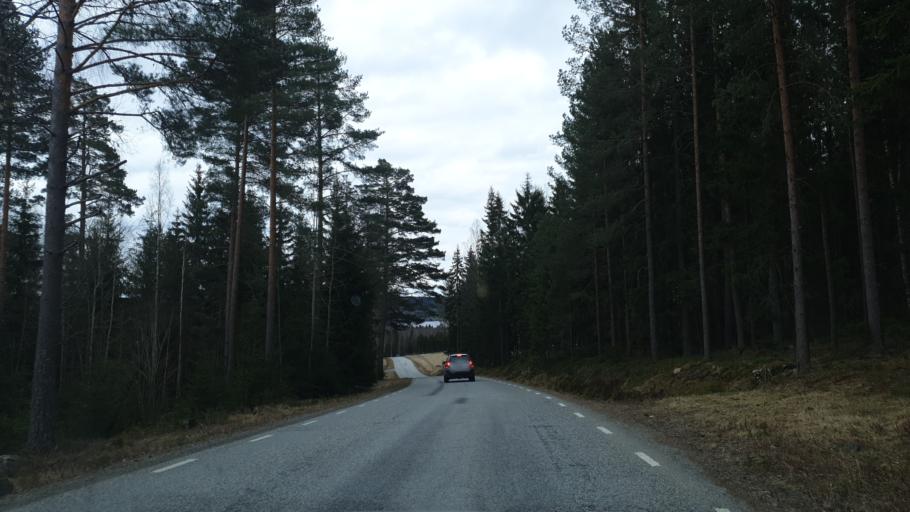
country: SE
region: OErebro
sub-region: Nora Kommun
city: As
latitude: 59.6143
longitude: 14.9797
